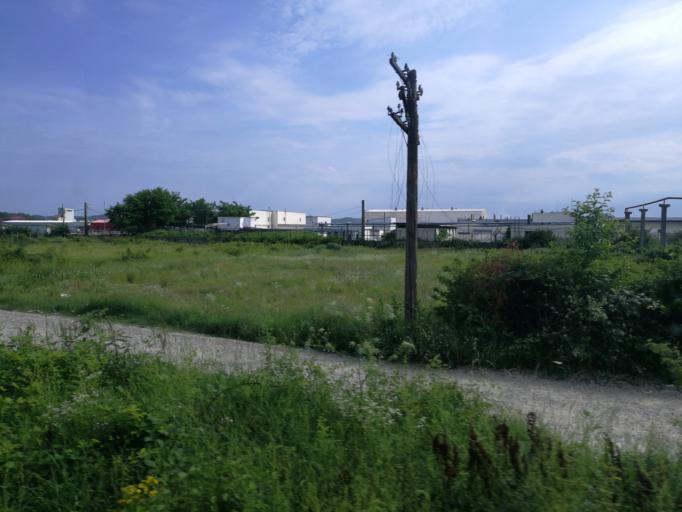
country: RO
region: Arges
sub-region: Comuna Bradu
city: Geamana
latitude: 44.8296
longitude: 24.9192
